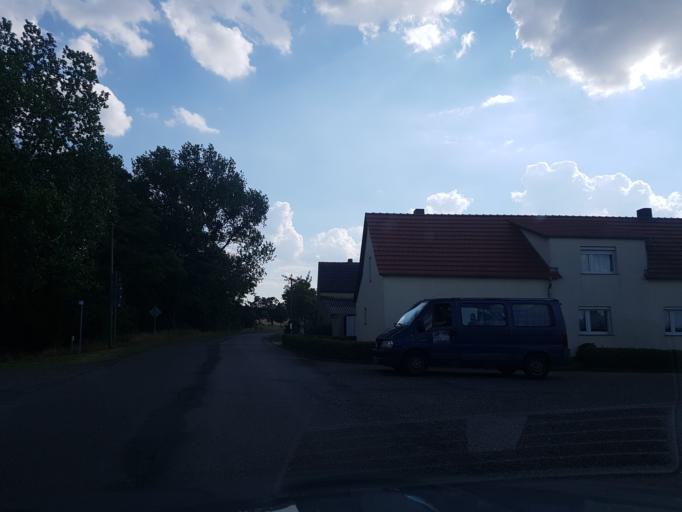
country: DE
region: Brandenburg
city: Schlieben
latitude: 51.6832
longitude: 13.3496
